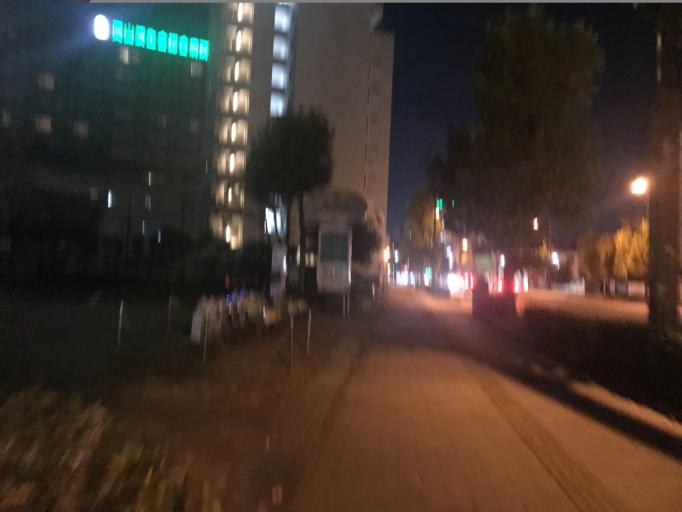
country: JP
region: Okayama
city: Okayama-shi
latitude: 34.6738
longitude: 133.9198
